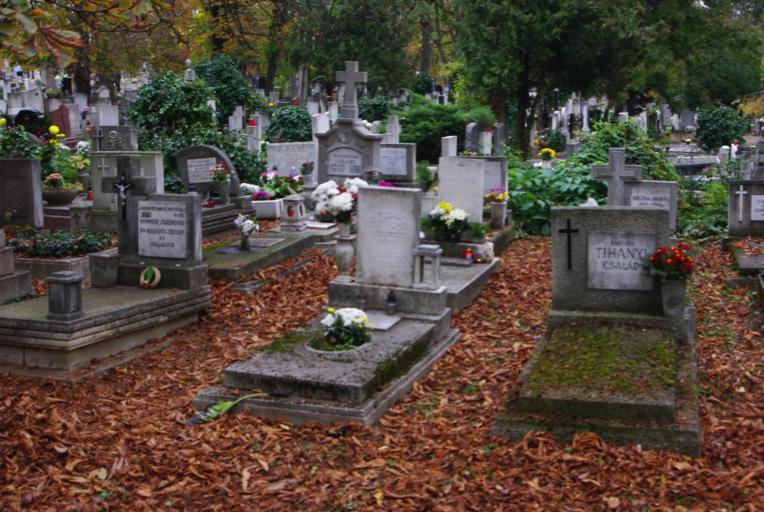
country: HU
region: Budapest
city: Budapest XII. keruelet
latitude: 47.4835
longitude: 19.0001
